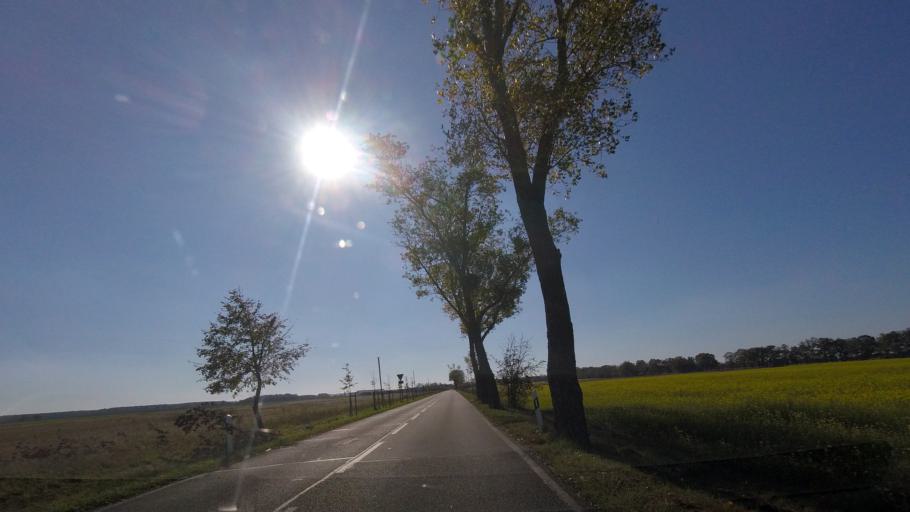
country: DE
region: Saxony-Anhalt
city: Muhlanger
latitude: 51.8458
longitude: 12.7663
